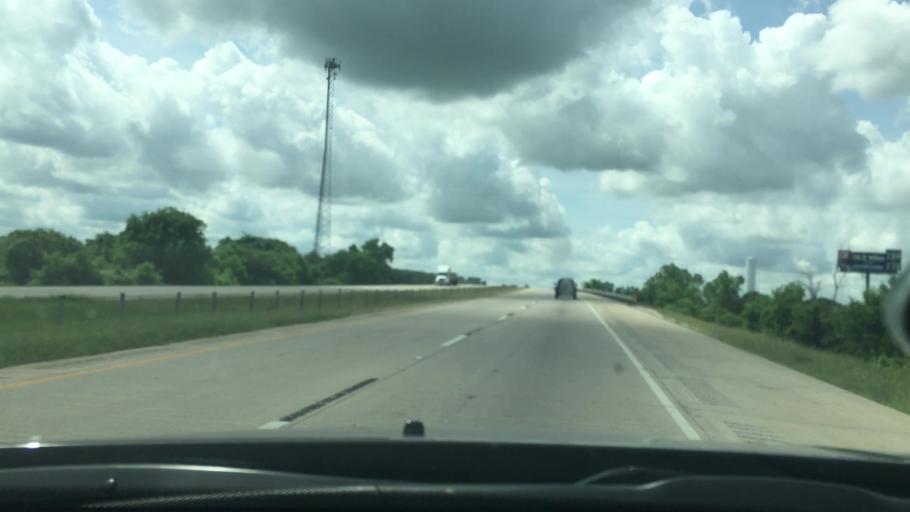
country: US
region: Oklahoma
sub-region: Love County
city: Marietta
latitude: 33.8394
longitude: -97.1332
